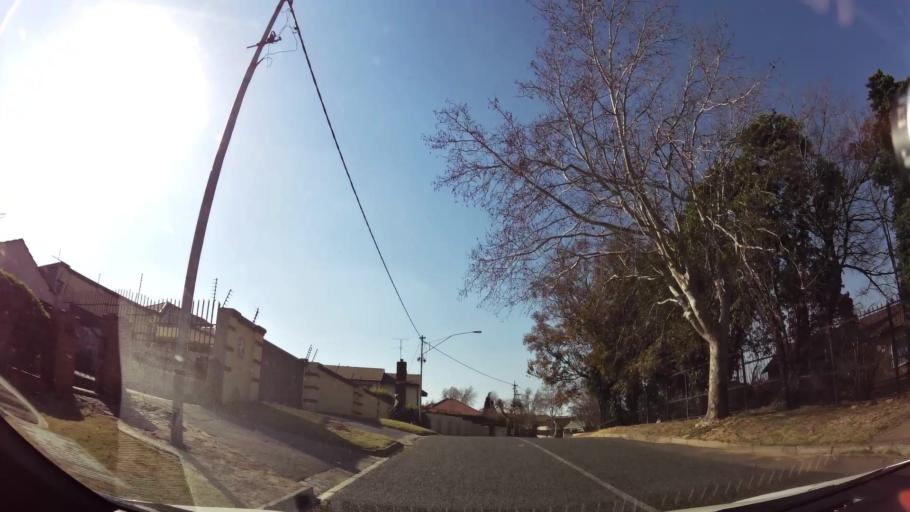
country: ZA
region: Gauteng
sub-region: City of Johannesburg Metropolitan Municipality
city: Johannesburg
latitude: -26.2601
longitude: 28.0659
